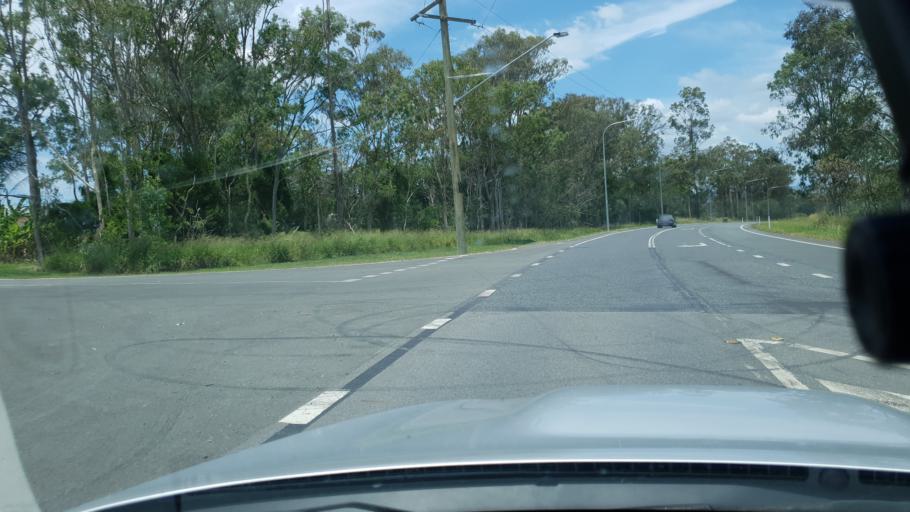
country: AU
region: Queensland
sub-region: Logan
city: North Maclean
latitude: -27.8157
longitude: 152.9968
